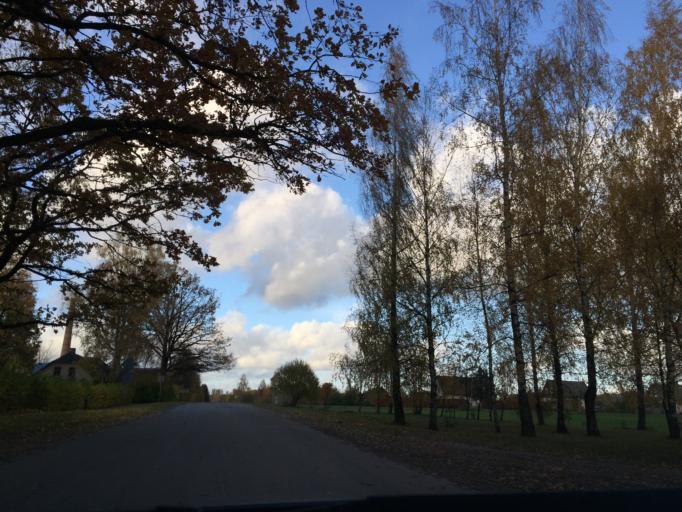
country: LV
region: Ogre
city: Jumprava
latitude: 56.7677
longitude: 25.0003
